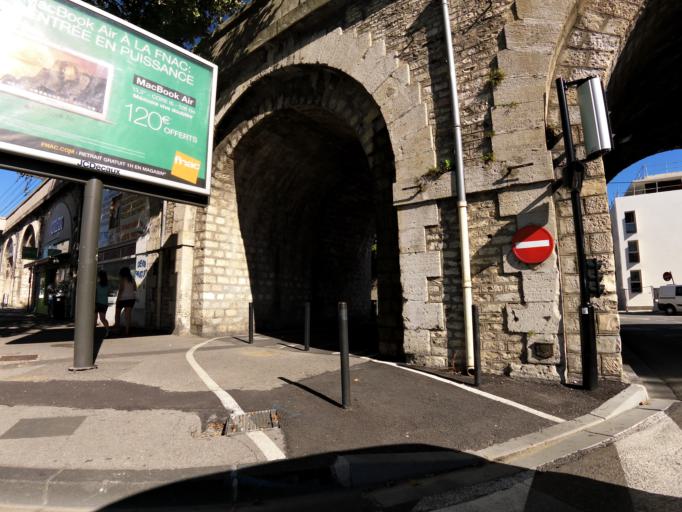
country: FR
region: Languedoc-Roussillon
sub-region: Departement du Gard
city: Nimes
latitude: 43.8295
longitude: 4.3620
